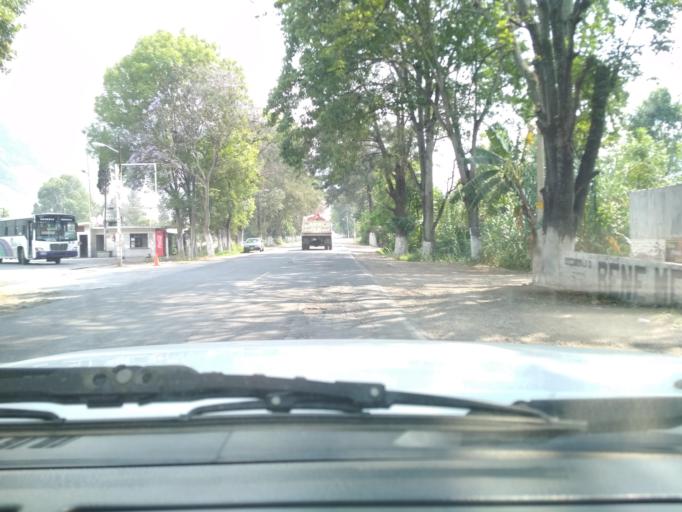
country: MX
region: Veracruz
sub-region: Acultzingo
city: Sierra de Agua
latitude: 18.7563
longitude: -97.2330
